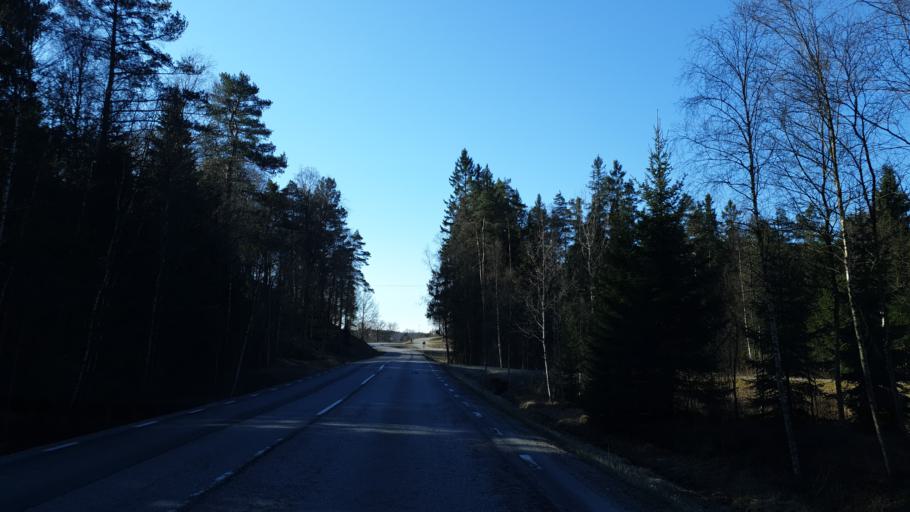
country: SE
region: Vaestra Goetaland
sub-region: Boras Kommun
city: Dalsjofors
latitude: 57.7391
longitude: 13.1054
